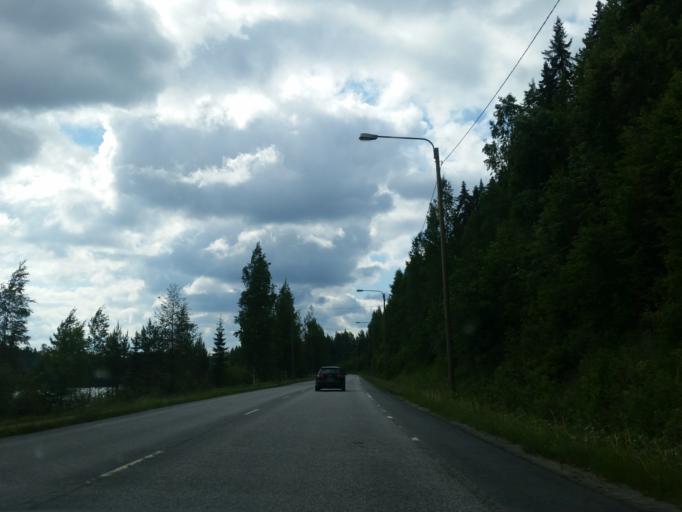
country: FI
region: Northern Savo
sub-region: Kuopio
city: Kuopio
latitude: 62.8437
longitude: 27.5533
